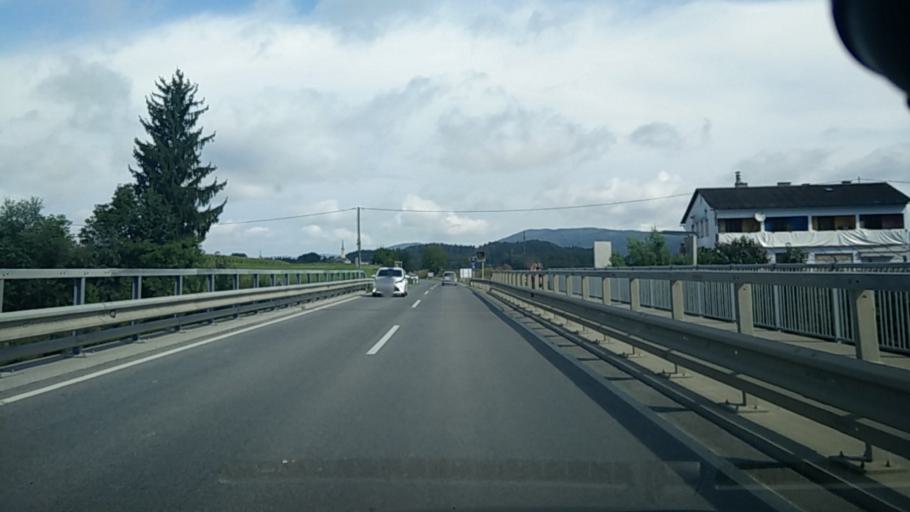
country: AT
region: Carinthia
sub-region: Politischer Bezirk Volkermarkt
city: Gallizien
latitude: 46.6208
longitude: 14.5471
